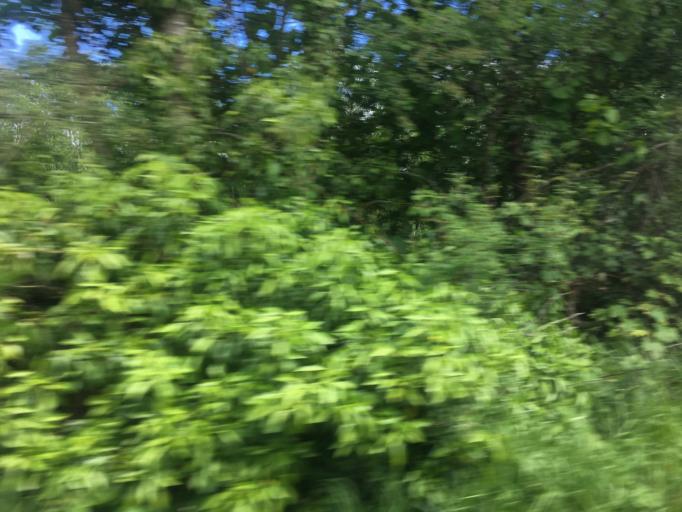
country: GB
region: Wales
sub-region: Carmarthenshire
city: Llansadwrn
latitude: 51.9700
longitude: -3.8756
